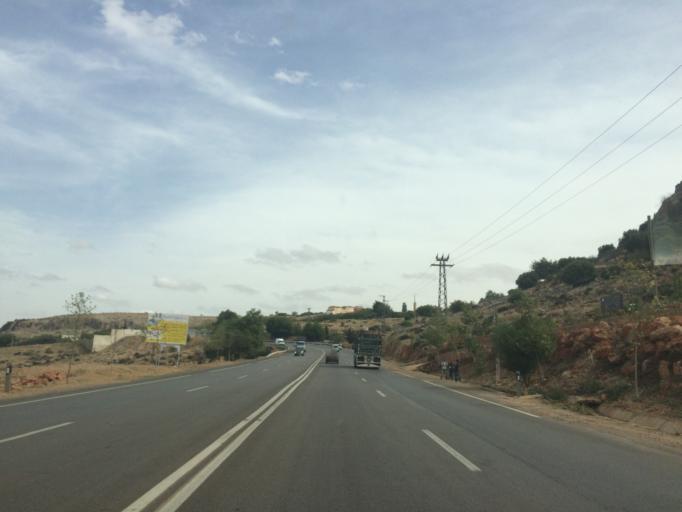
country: MA
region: Meknes-Tafilalet
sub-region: El-Hajeb
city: El Hajeb
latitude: 33.6916
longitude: -5.3875
